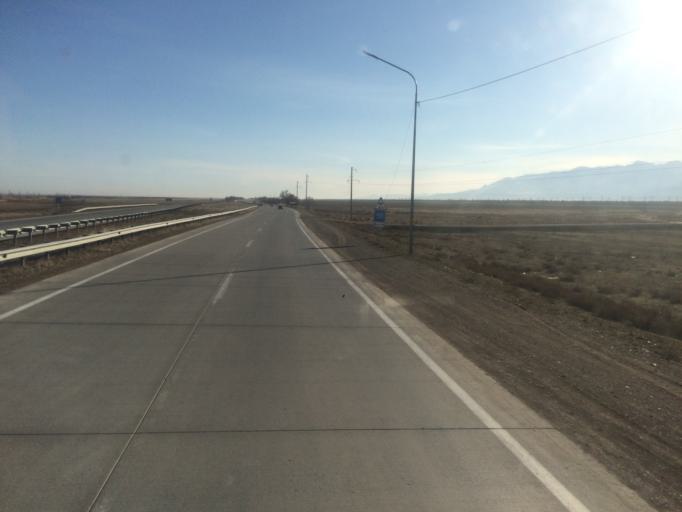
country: KZ
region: Zhambyl
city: Sarykemer
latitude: 43.0083
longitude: 71.8125
